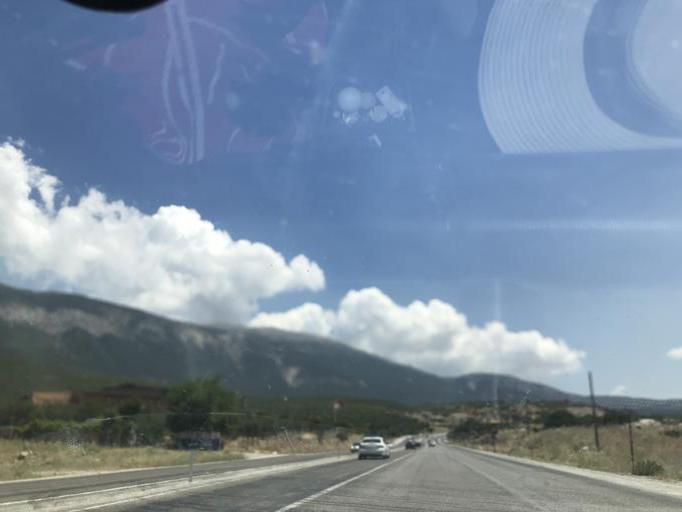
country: TR
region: Denizli
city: Honaz
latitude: 37.6946
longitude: 29.2093
